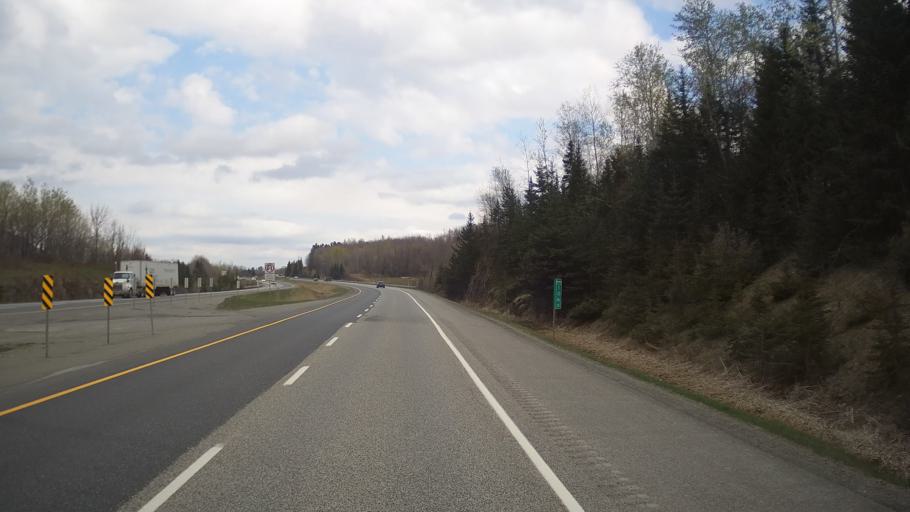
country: CA
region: Quebec
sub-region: Estrie
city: Magog
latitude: 45.2964
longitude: -72.3003
